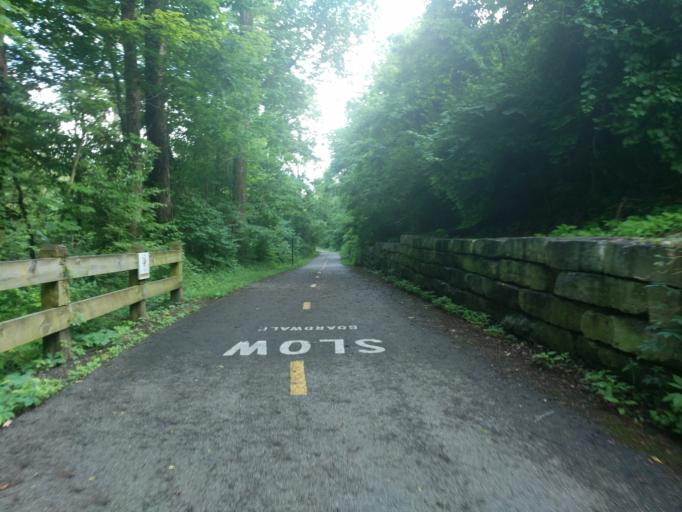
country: US
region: Ohio
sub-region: Franklin County
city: Minerva Park
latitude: 40.0420
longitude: -82.9346
